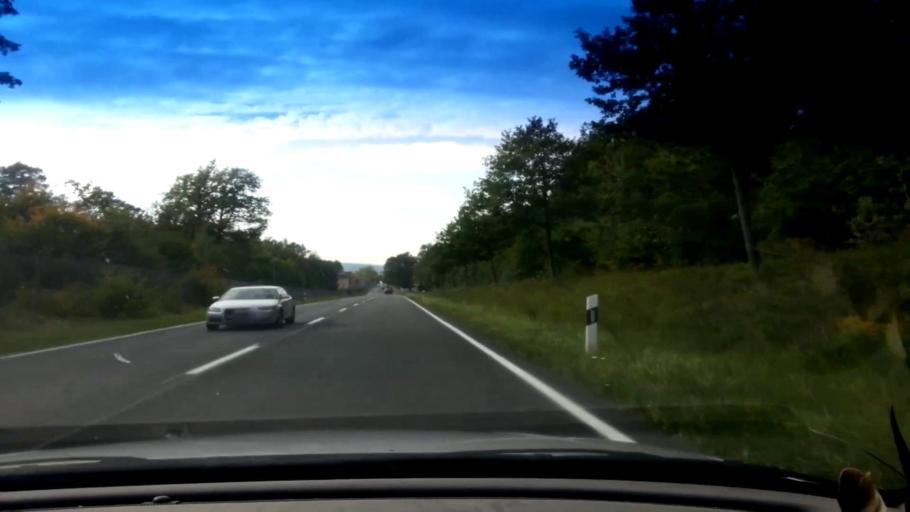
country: DE
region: Bavaria
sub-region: Upper Franconia
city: Bamberg
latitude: 49.8893
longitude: 10.9325
